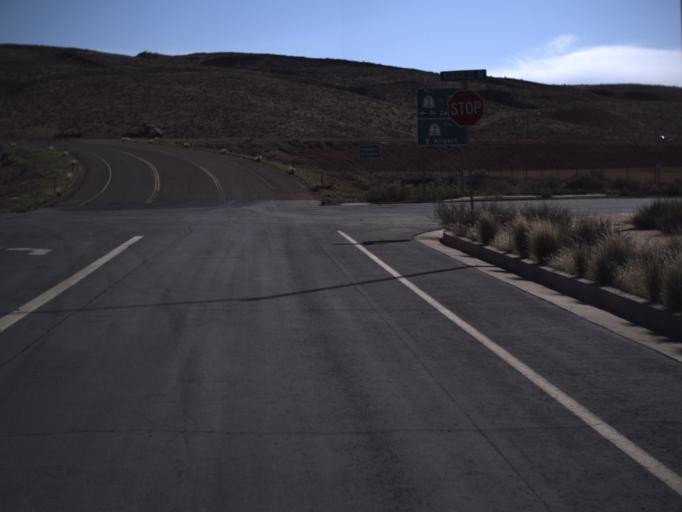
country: US
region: Utah
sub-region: Washington County
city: Saint George
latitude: 37.0225
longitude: -113.6035
